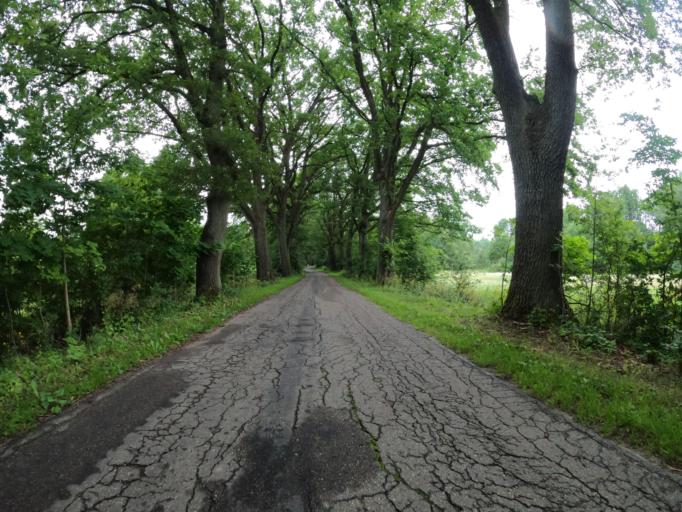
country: PL
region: West Pomeranian Voivodeship
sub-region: Powiat koszalinski
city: Bobolice
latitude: 53.9115
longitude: 16.5053
